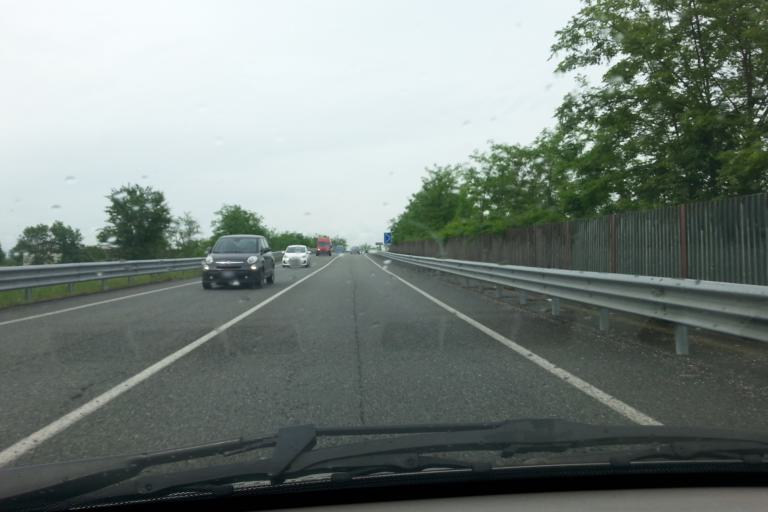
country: IT
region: Piedmont
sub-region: Provincia di Torino
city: Alpignano
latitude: 45.1179
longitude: 7.5157
